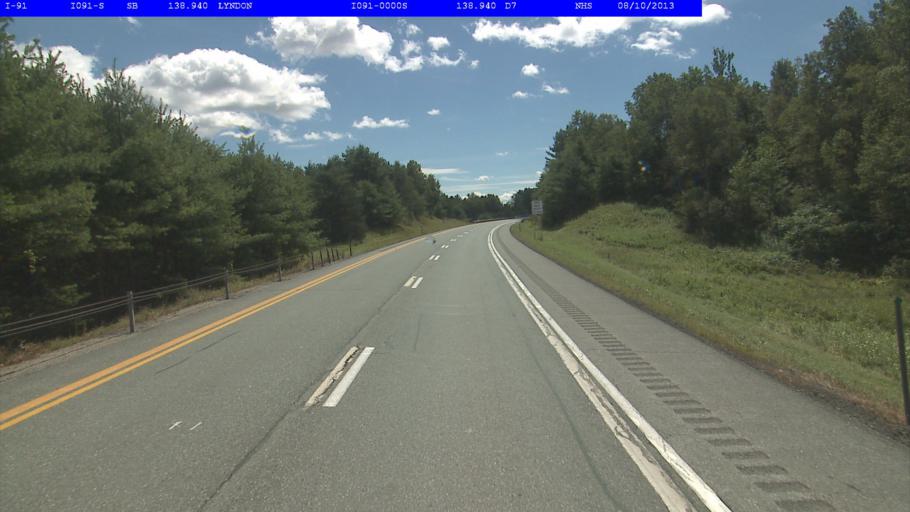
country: US
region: Vermont
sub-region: Caledonia County
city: Lyndonville
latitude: 44.5410
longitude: -72.0214
